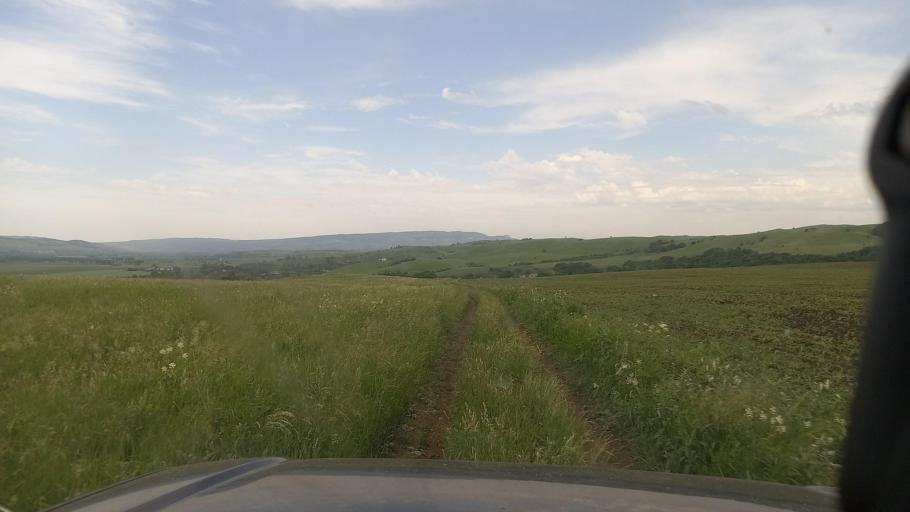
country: RU
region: Krasnodarskiy
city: Peredovaya
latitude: 44.0787
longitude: 41.3398
